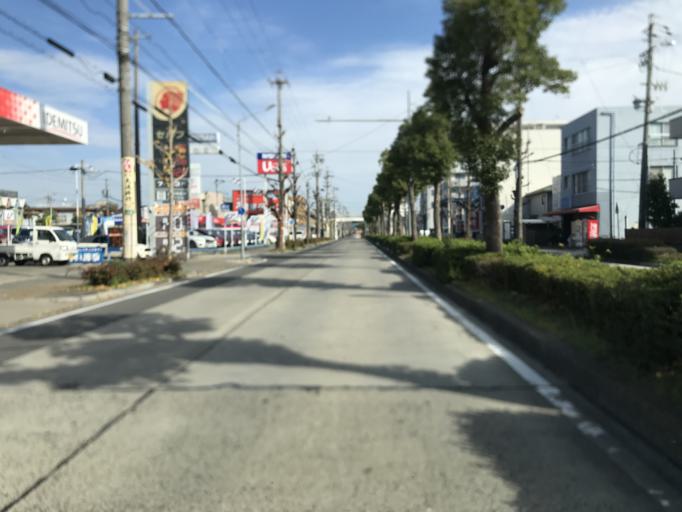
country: JP
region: Aichi
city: Nagoya-shi
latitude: 35.2047
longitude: 136.9250
